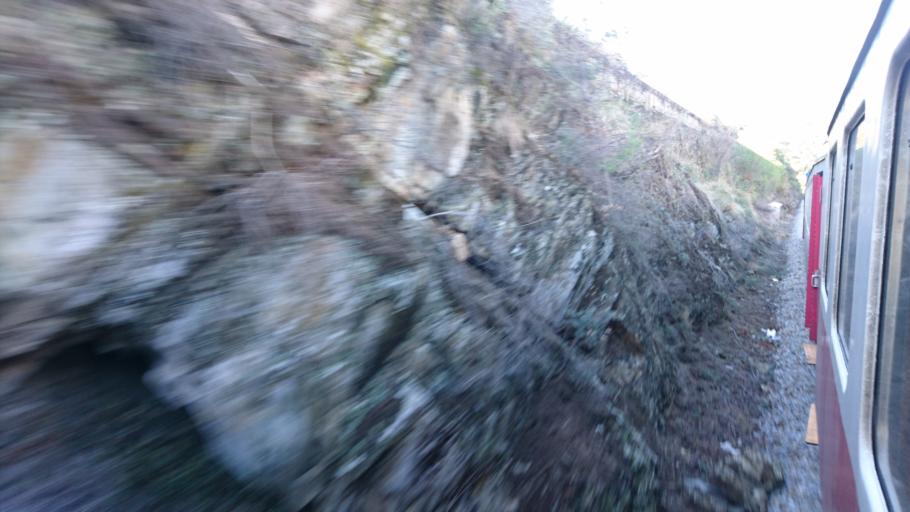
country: PT
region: Guarda
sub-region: Vila Nova de Foz Coa
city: Vila Nova de Foz Coa
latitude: 41.1346
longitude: -7.2122
